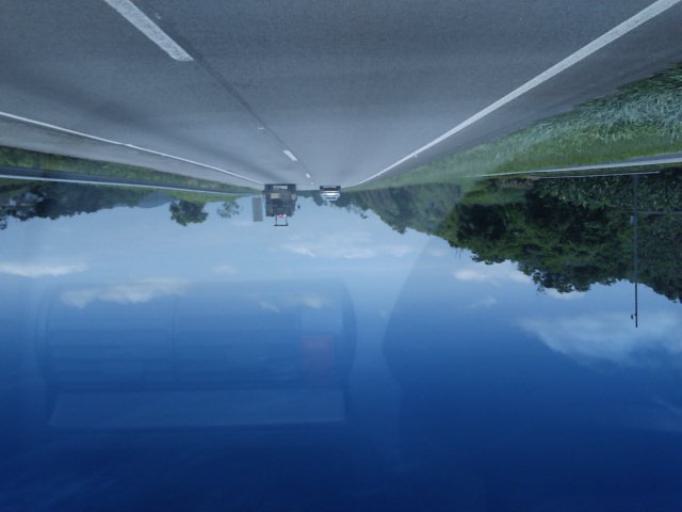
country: BR
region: Sao Paulo
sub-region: Miracatu
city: Miracatu
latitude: -24.2847
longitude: -47.4386
